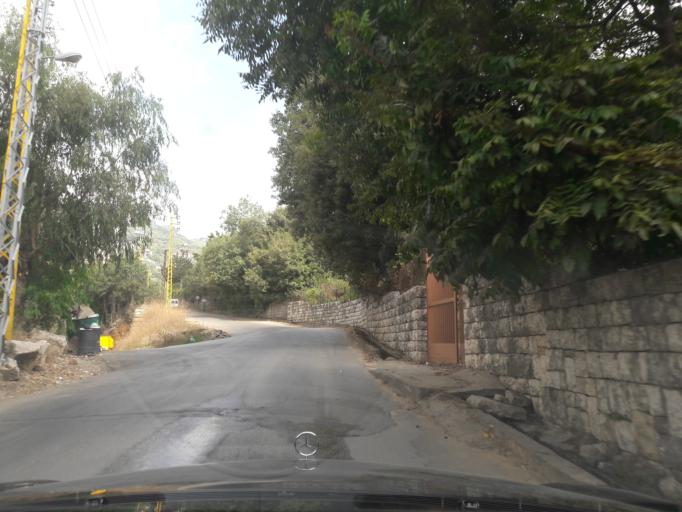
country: LB
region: Mont-Liban
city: Djounie
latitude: 33.9266
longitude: 35.6644
